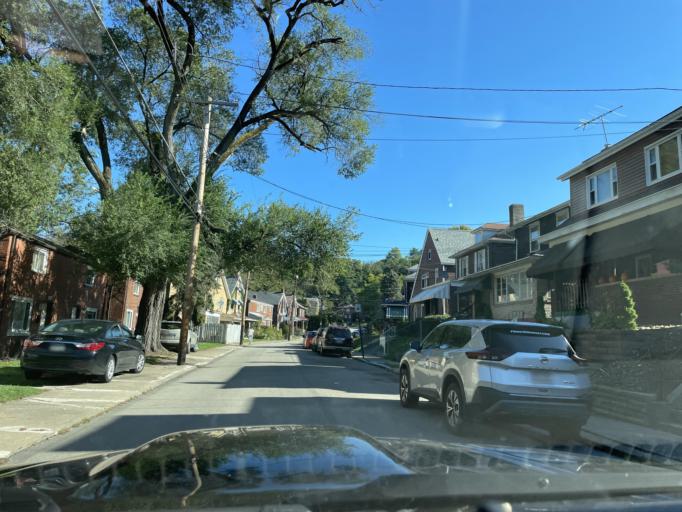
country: US
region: Pennsylvania
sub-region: Allegheny County
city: Wilkinsburg
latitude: 40.4386
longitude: -79.8706
